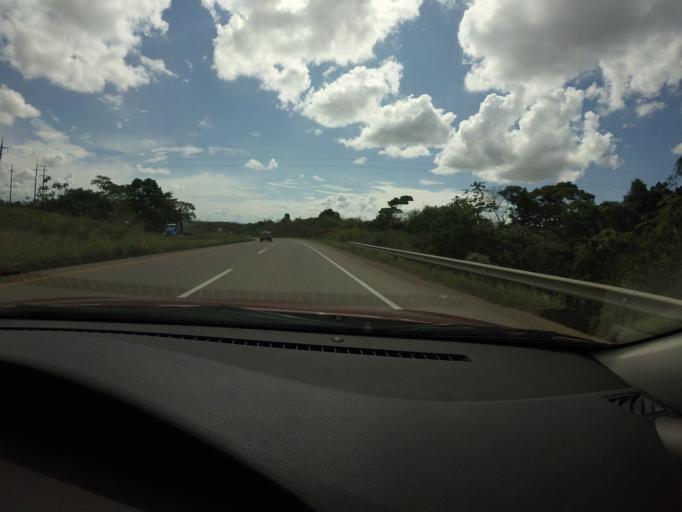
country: CO
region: Antioquia
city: Puerto Triunfo
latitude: 5.7874
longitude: -74.6045
